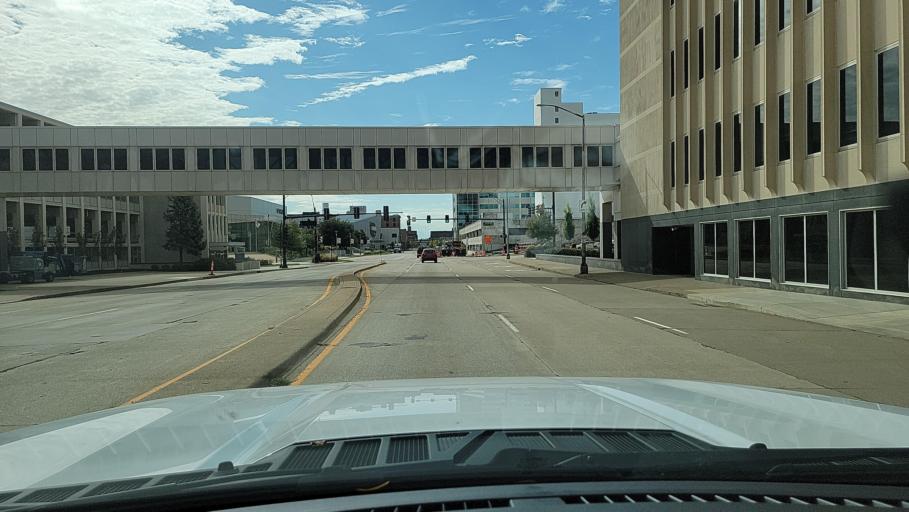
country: US
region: Illinois
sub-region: Peoria County
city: Peoria
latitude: 40.6914
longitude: -89.5877
